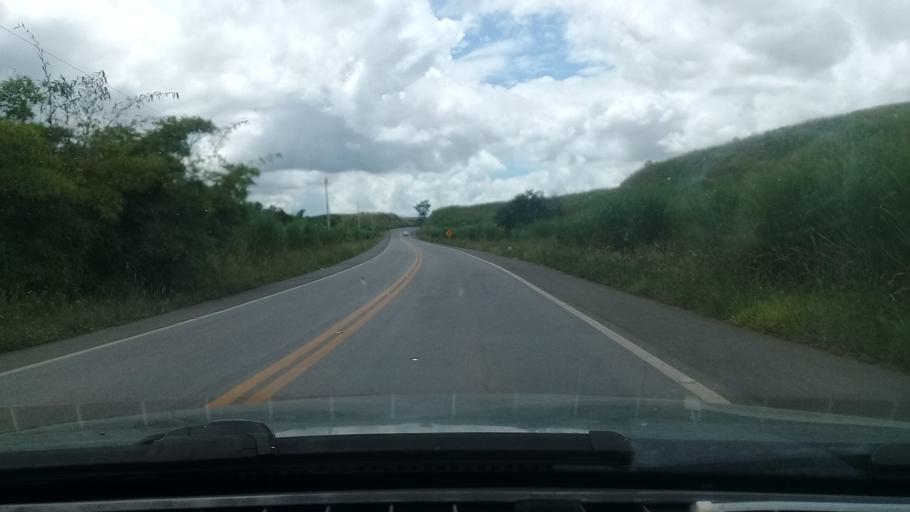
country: BR
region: Pernambuco
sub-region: Vicencia
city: Vicencia
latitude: -7.6336
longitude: -35.2518
